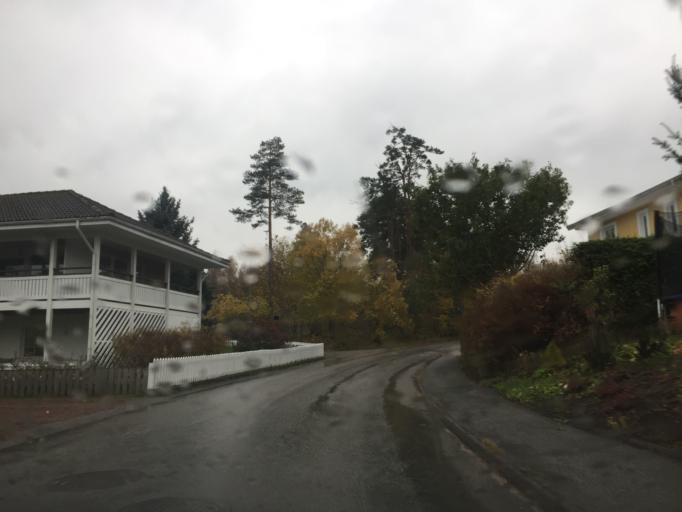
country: SE
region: Vaestra Goetaland
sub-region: Trollhattan
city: Trollhattan
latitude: 58.3023
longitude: 12.2858
